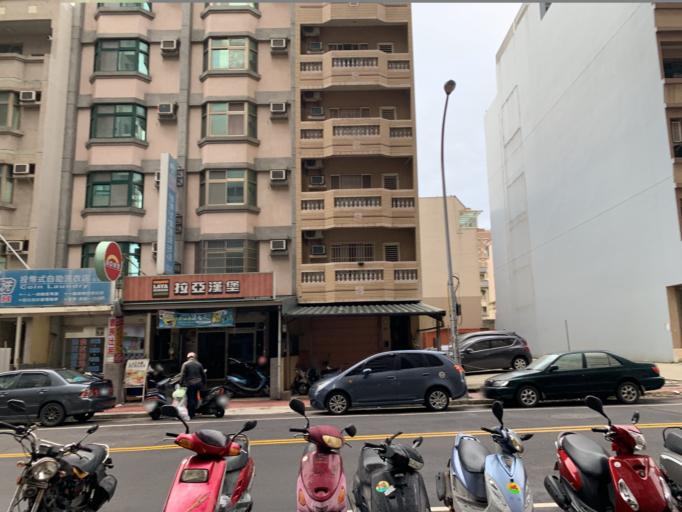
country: TW
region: Taiwan
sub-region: Hsinchu
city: Zhubei
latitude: 24.8172
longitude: 121.0191
